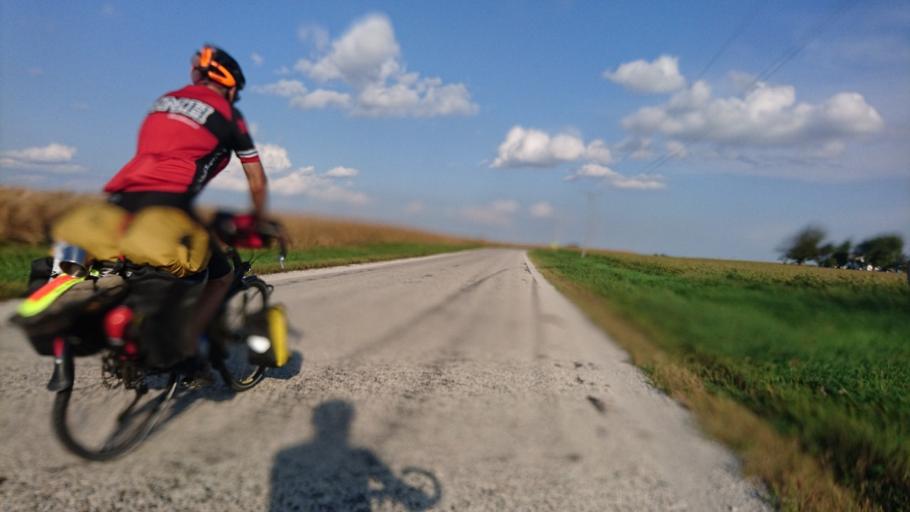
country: US
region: Illinois
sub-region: Logan County
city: Atlanta
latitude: 40.2598
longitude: -89.2085
